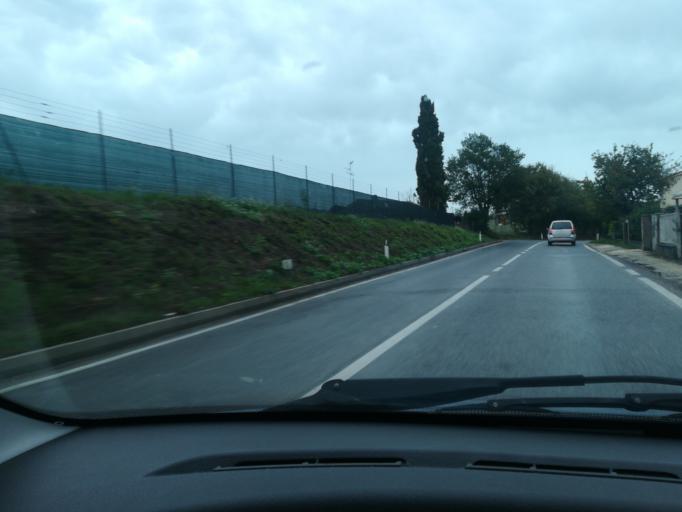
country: IT
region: The Marches
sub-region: Provincia di Macerata
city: Santa Maria Apparente
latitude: 43.2946
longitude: 13.6691
